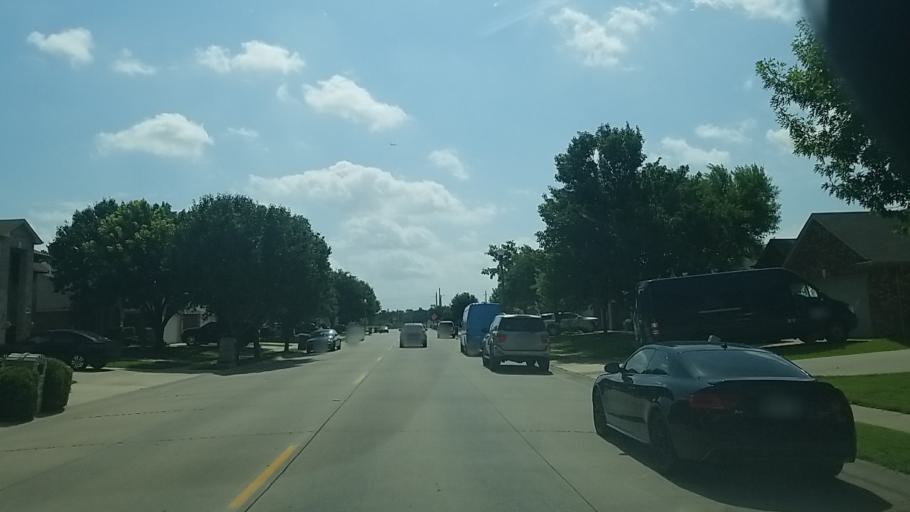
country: US
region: Texas
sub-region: Denton County
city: Corinth
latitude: 33.1419
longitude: -97.1080
